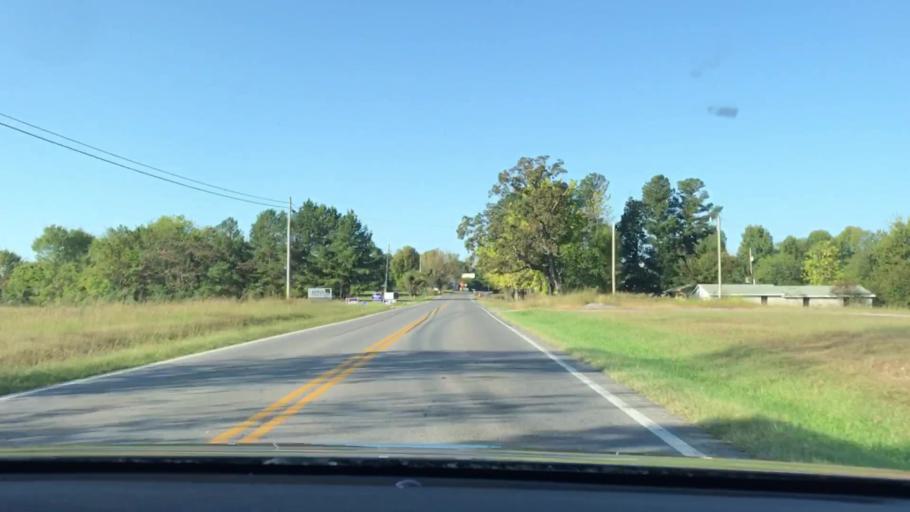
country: US
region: Kentucky
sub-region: Trigg County
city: Cadiz
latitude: 36.8130
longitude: -87.8834
